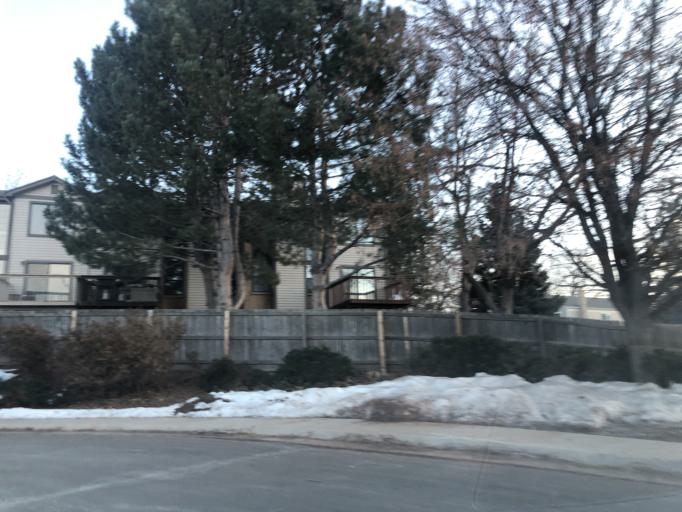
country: US
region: Colorado
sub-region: Adams County
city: Aurora
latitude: 39.7022
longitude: -104.8022
